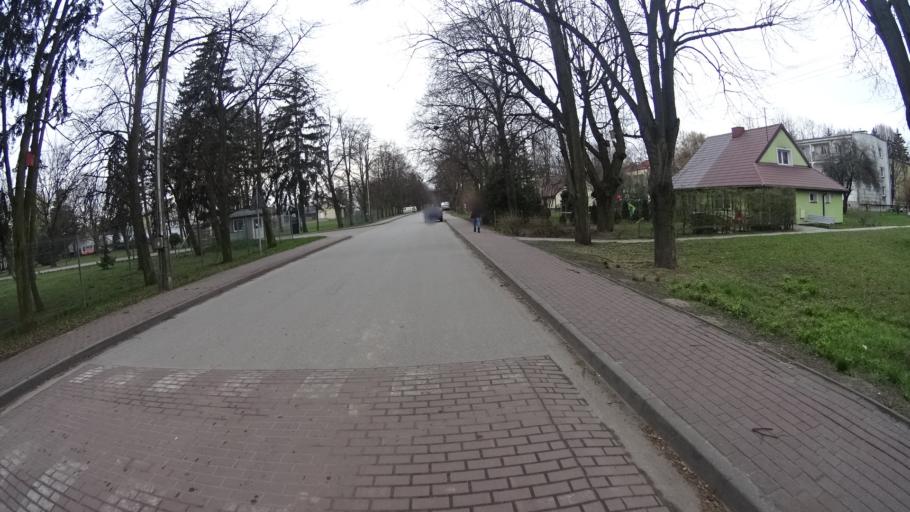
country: PL
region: Masovian Voivodeship
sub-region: Powiat warszawski zachodni
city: Blonie
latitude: 52.2155
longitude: 20.6445
